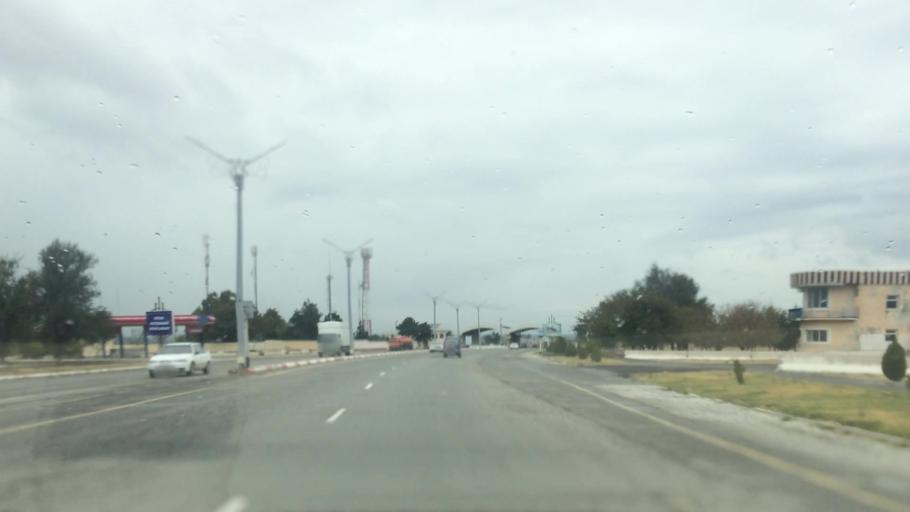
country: UZ
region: Samarqand
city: Bulung'ur
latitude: 39.8513
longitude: 67.4628
